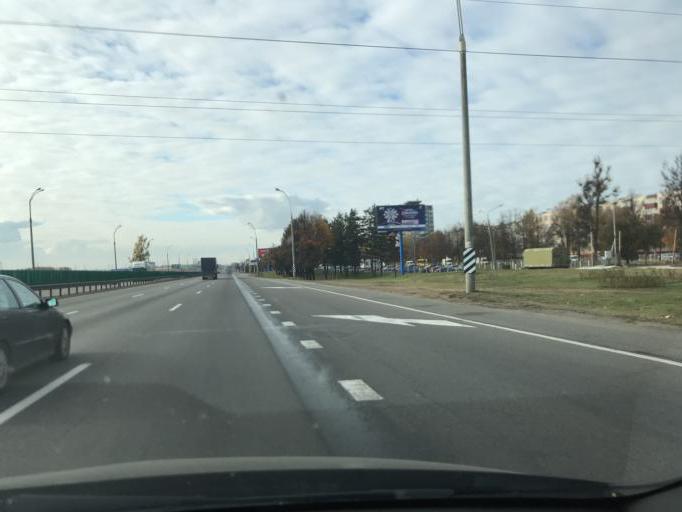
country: BY
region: Minsk
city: Hatava
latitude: 53.8337
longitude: 27.6292
